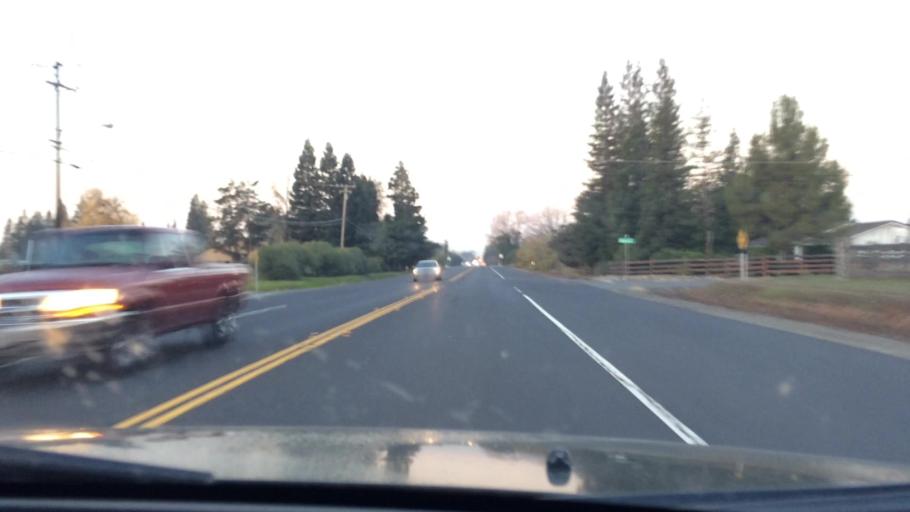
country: US
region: California
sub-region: Sacramento County
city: Vineyard
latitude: 38.4382
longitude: -121.3604
